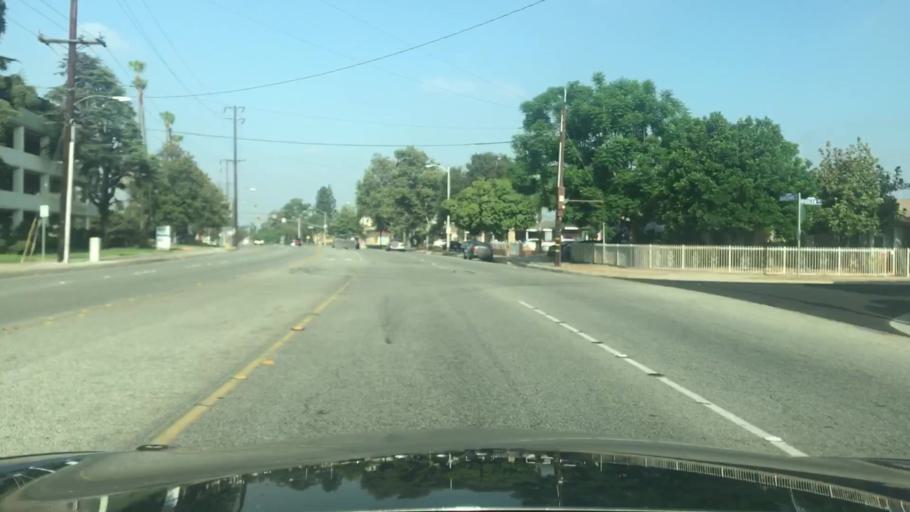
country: US
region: California
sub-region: Los Angeles County
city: Bellflower
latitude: 33.9040
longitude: -118.1314
